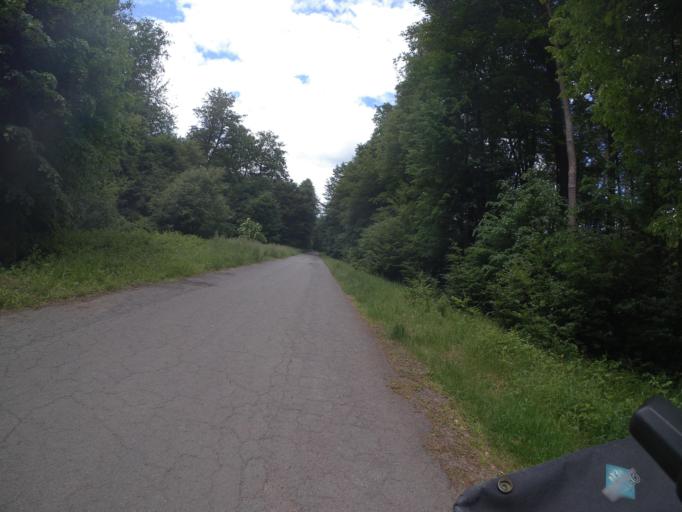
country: DE
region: Rheinland-Pfalz
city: Rodenbach
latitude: 49.4654
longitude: 7.6731
